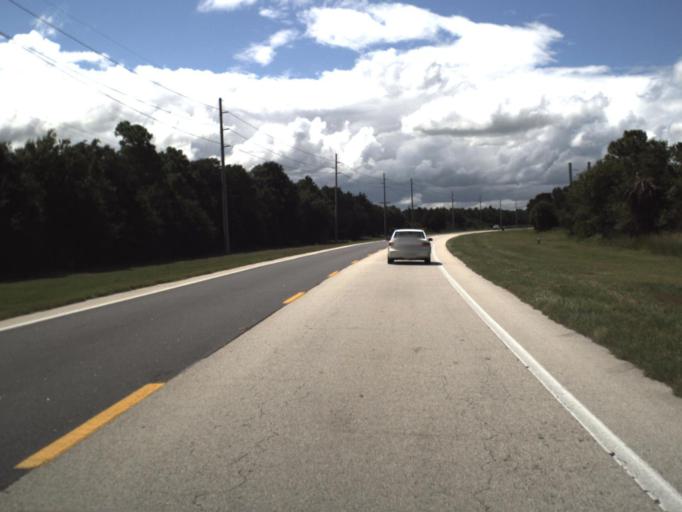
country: US
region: Florida
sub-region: Polk County
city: Mulberry
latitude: 27.7876
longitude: -81.9828
